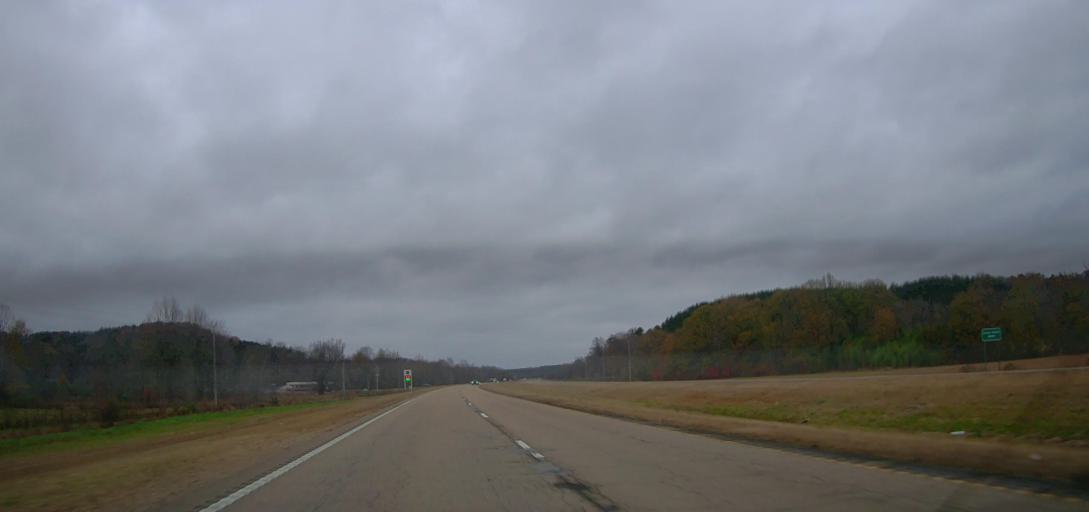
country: US
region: Mississippi
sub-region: Alcorn County
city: Corinth
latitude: 34.9344
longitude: -88.7714
